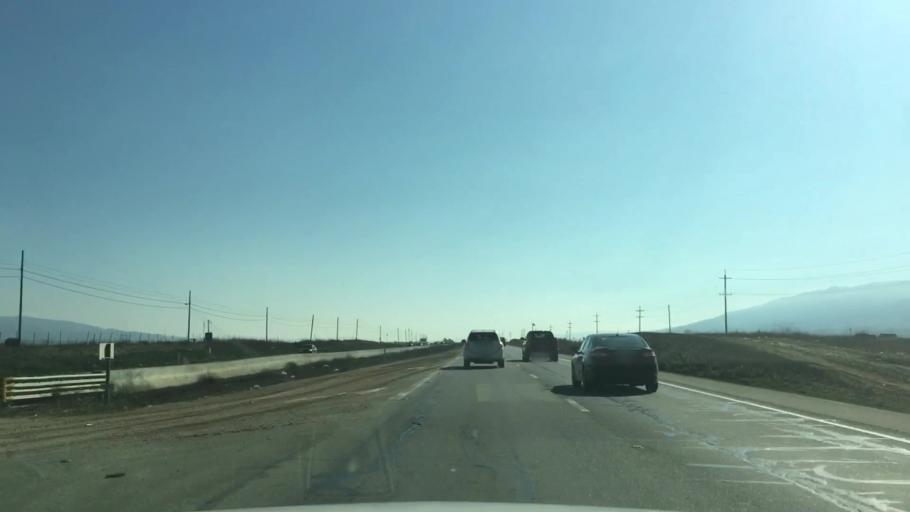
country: US
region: California
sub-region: Monterey County
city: Chualar
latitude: 36.5589
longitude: -121.5078
